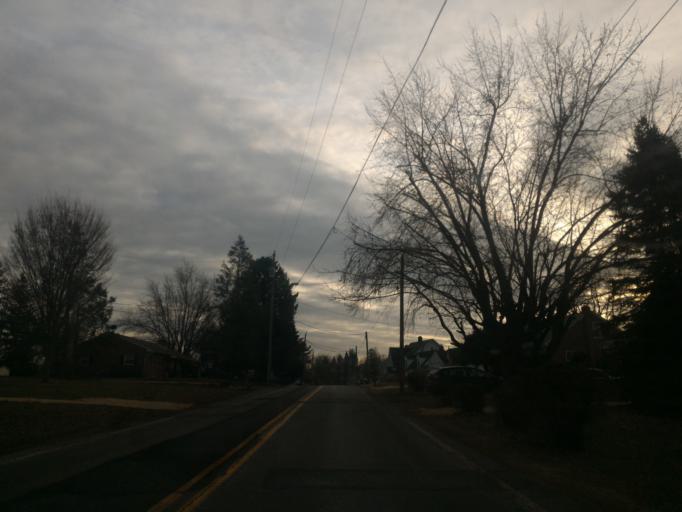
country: US
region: Pennsylvania
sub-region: York County
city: Jacobus
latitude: 39.8847
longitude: -76.7076
